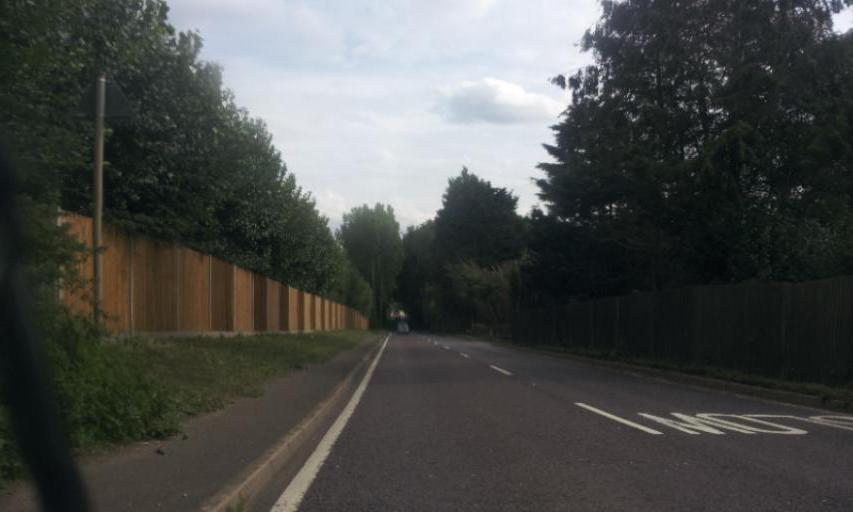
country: GB
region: England
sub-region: Kent
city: Kings Hill
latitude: 51.2608
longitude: 0.3654
